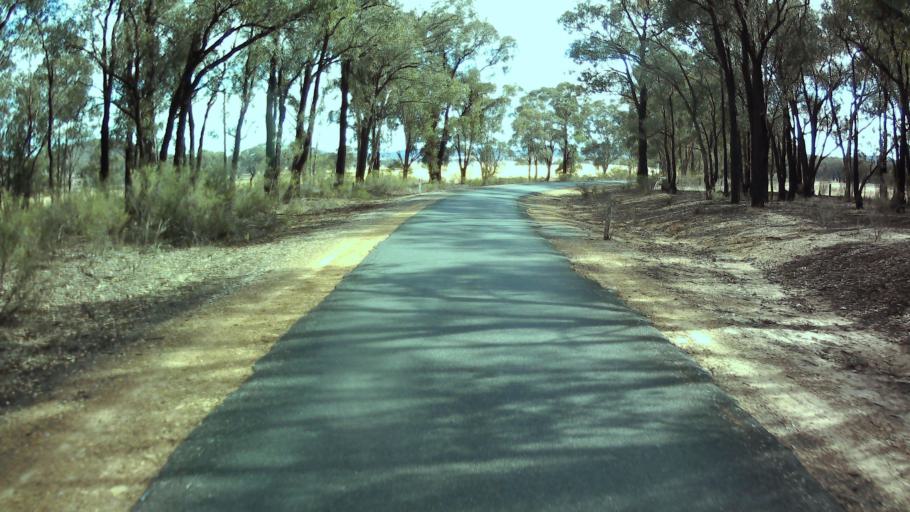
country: AU
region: New South Wales
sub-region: Weddin
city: Grenfell
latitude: -33.8544
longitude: 148.2178
